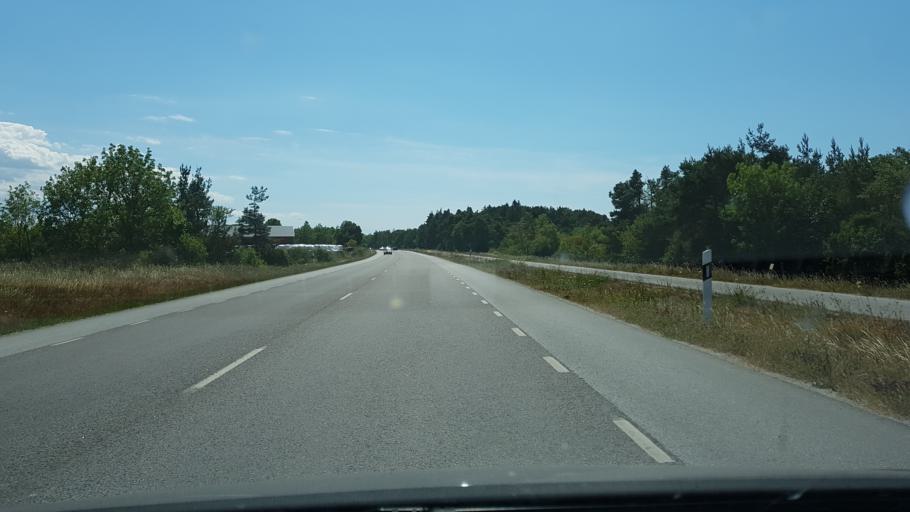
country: SE
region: Gotland
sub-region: Gotland
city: Vibble
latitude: 57.5155
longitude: 18.1583
